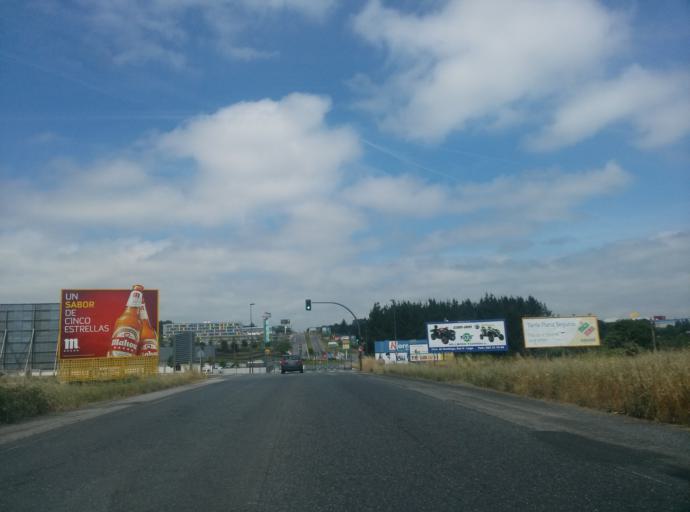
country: ES
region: Galicia
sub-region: Provincia de Lugo
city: Lugo
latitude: 43.0341
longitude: -7.5644
